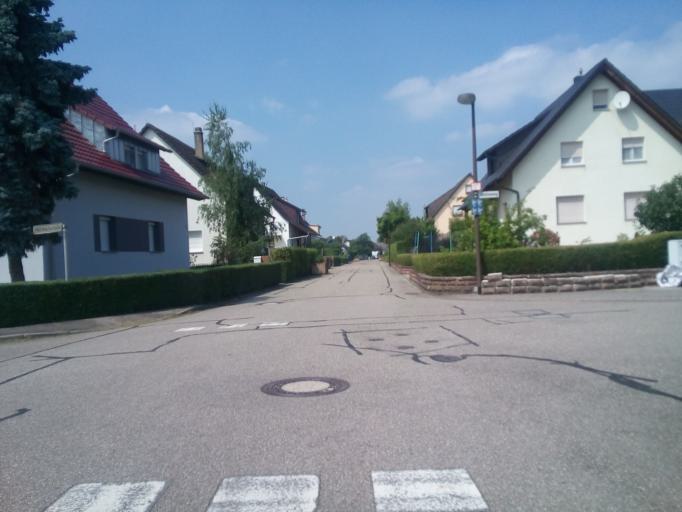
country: FR
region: Alsace
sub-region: Departement du Bas-Rhin
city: Kilstett
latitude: 48.6408
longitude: 7.8874
